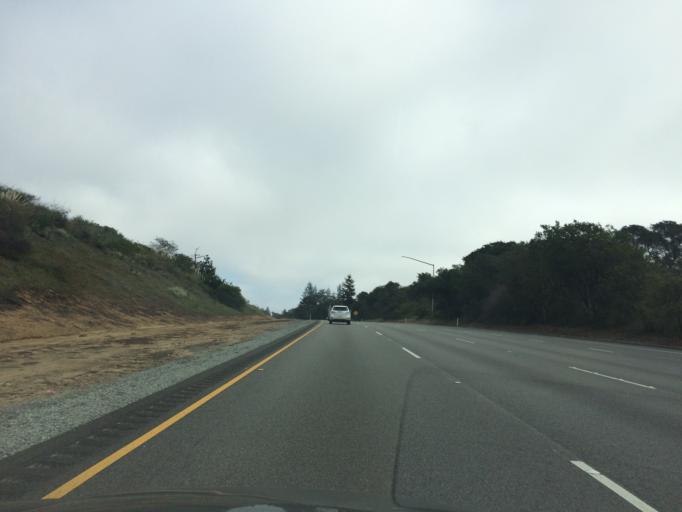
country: US
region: California
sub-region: Santa Cruz County
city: Aptos Hills-Larkin Valley
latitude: 36.9399
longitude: -121.8373
